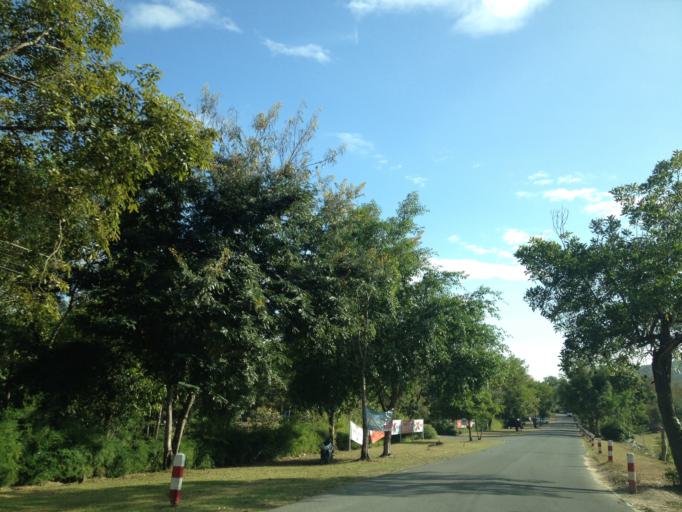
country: TH
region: Chiang Mai
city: Chiang Mai
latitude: 18.8692
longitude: 98.9450
